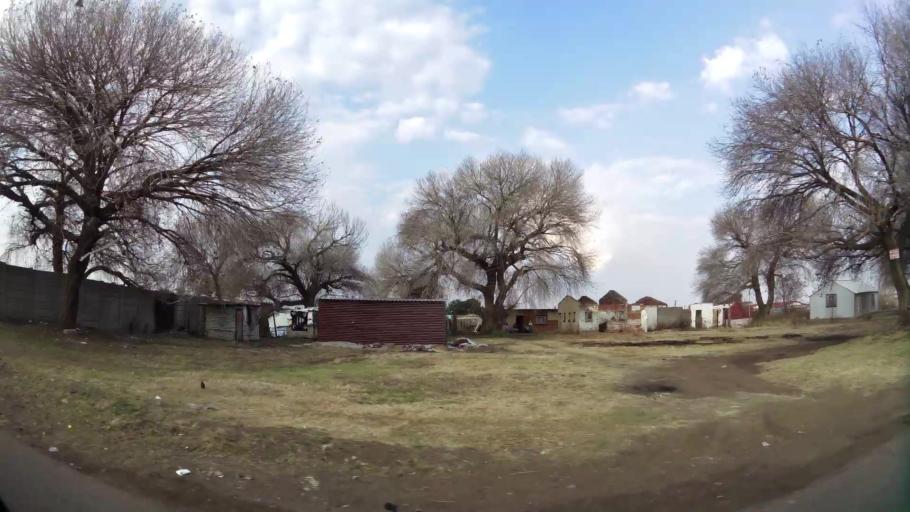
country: ZA
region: Gauteng
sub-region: Sedibeng District Municipality
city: Vanderbijlpark
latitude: -26.6908
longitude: 27.8770
